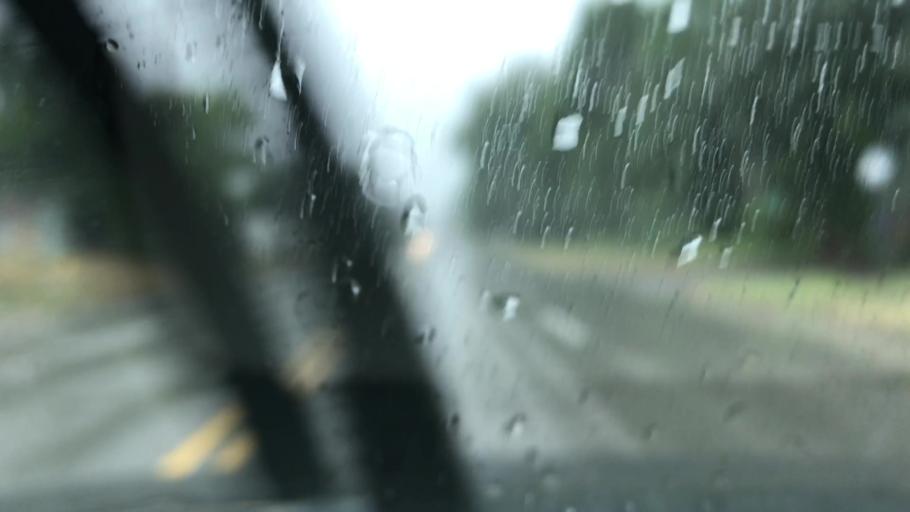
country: US
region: Michigan
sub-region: Kent County
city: Wyoming
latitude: 42.8935
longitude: -85.7244
